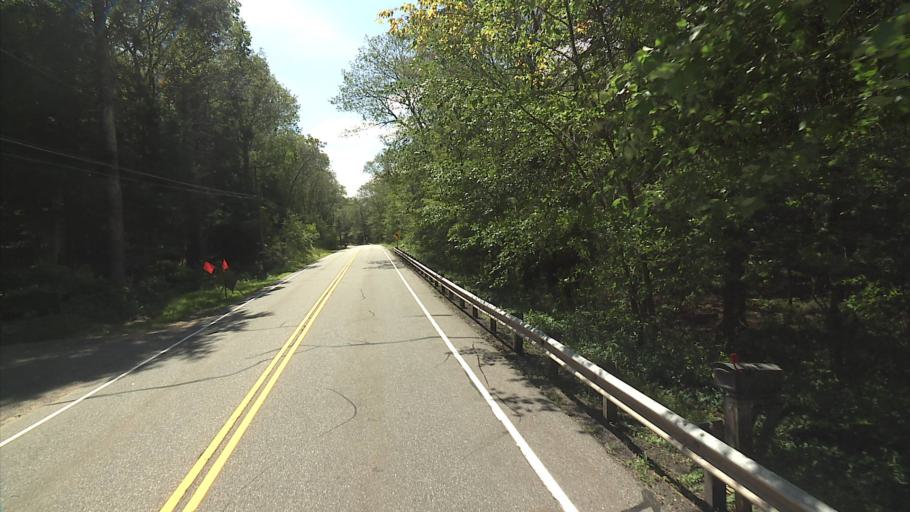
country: US
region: Connecticut
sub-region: Windham County
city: South Woodstock
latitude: 41.9268
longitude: -72.0830
